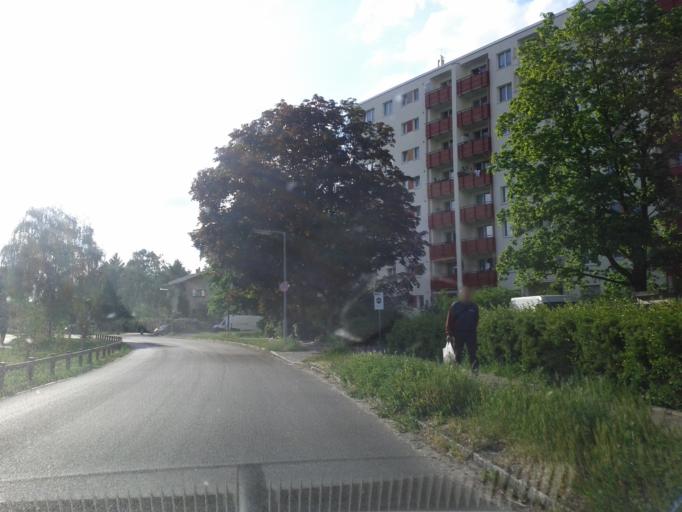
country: DE
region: Berlin
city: Falkenhagener Feld
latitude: 52.5434
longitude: 13.1775
